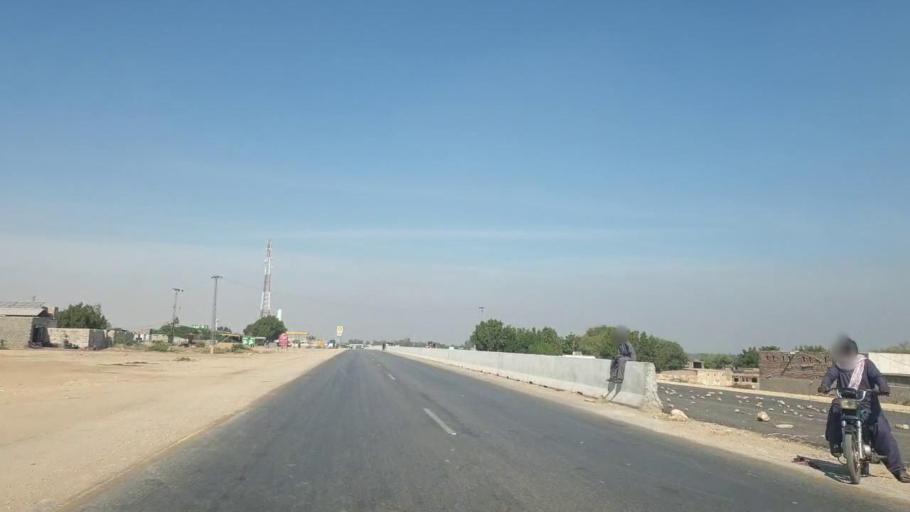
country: PK
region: Sindh
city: Hala
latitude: 25.7020
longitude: 68.2957
